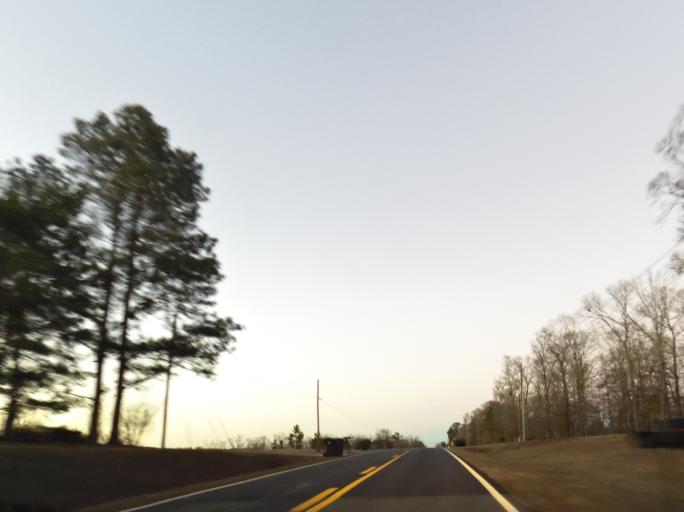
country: US
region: Georgia
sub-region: Peach County
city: Byron
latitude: 32.6292
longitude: -83.7573
